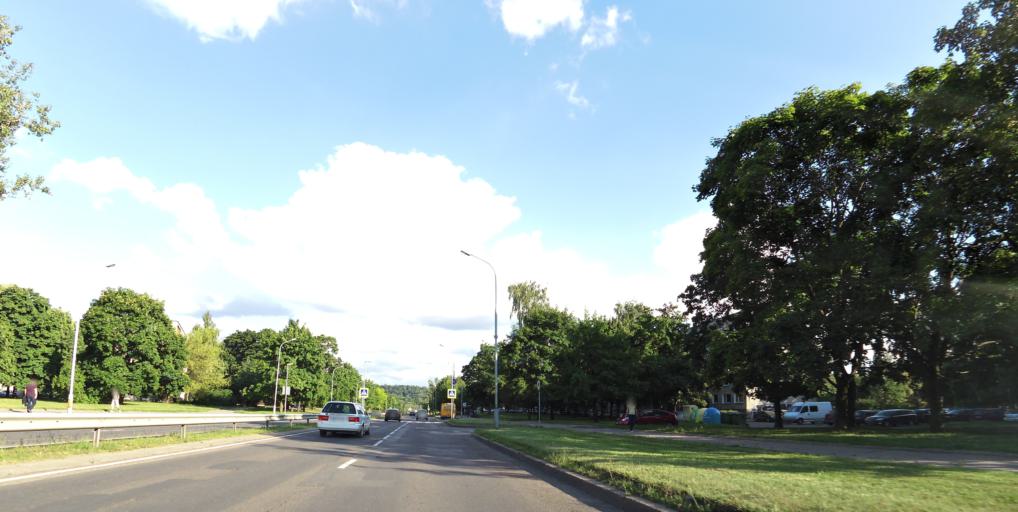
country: LT
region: Vilnius County
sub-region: Vilnius
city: Vilnius
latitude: 54.7009
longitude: 25.2920
